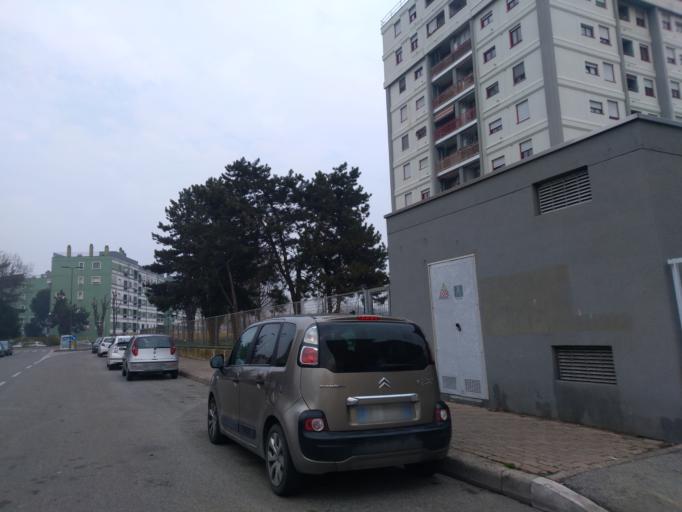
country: IT
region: Lombardy
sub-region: Citta metropolitana di Milano
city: Figino
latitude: 45.4778
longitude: 9.0904
